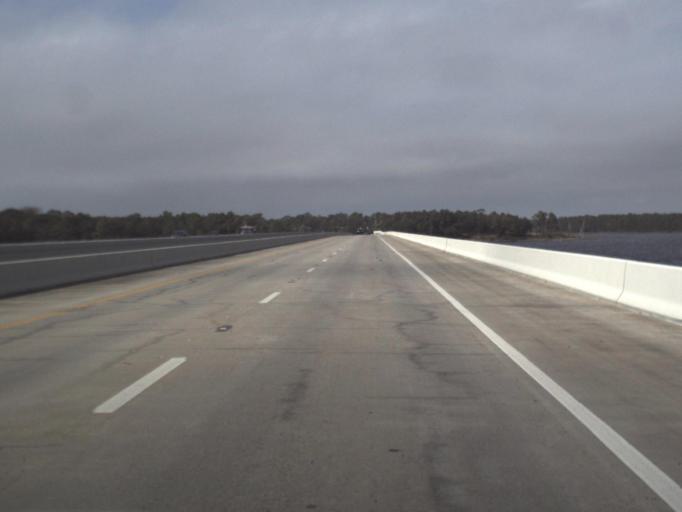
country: US
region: Florida
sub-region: Bay County
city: Laguna Beach
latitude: 30.2724
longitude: -85.9837
